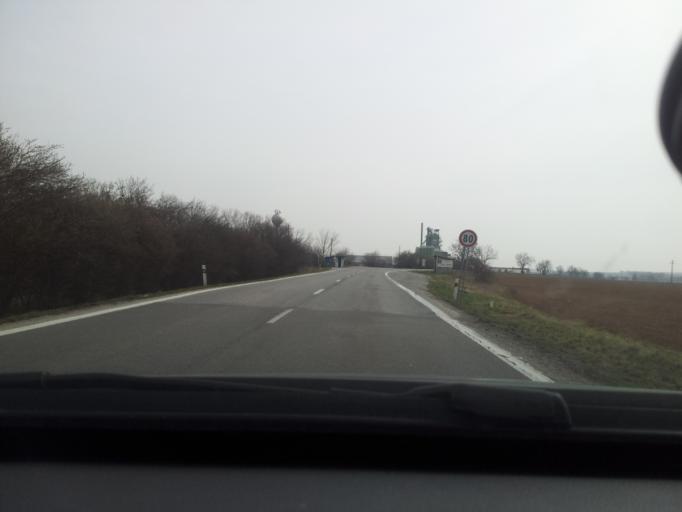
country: SK
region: Nitriansky
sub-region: Okres Nitra
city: Vrable
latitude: 48.2906
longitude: 18.2087
